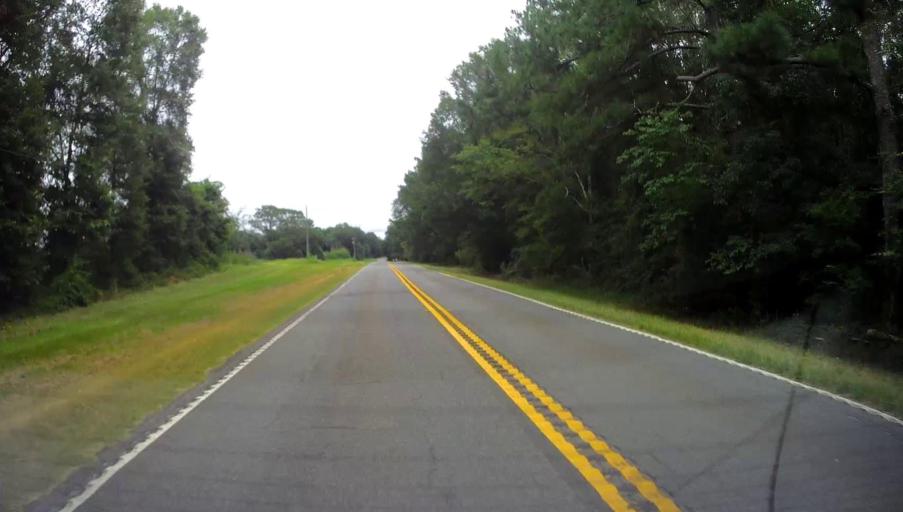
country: US
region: Georgia
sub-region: Macon County
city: Montezuma
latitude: 32.2931
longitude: -83.9108
